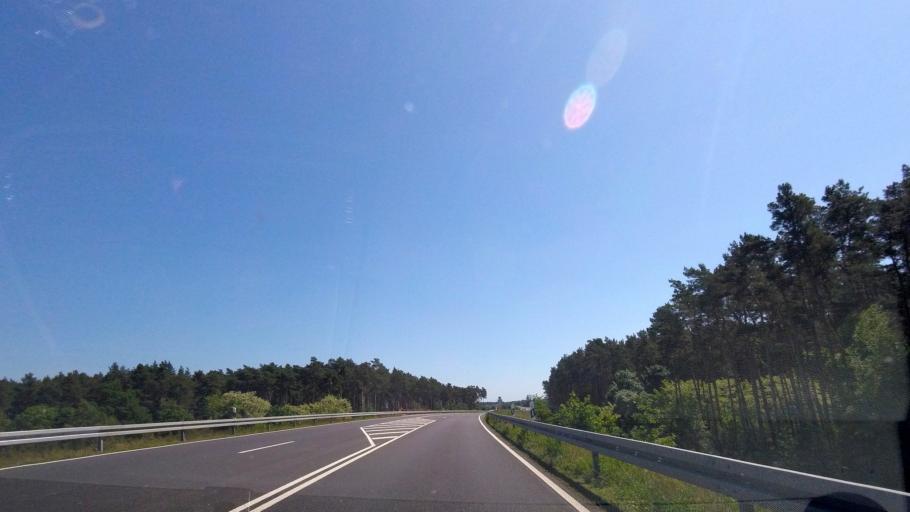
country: DE
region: Brandenburg
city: Luckenwalde
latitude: 52.1253
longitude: 13.1879
